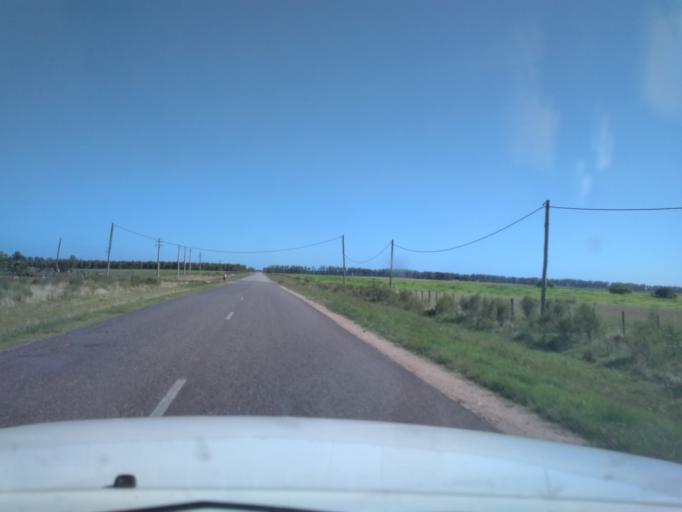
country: UY
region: Canelones
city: San Ramon
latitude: -34.1547
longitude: -55.9464
